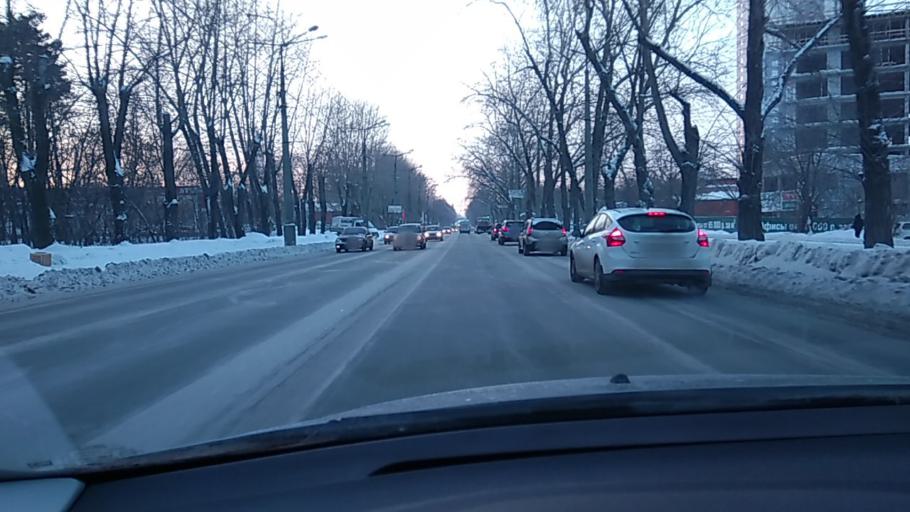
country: RU
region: Sverdlovsk
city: Yekaterinburg
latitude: 56.8874
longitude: 60.6096
